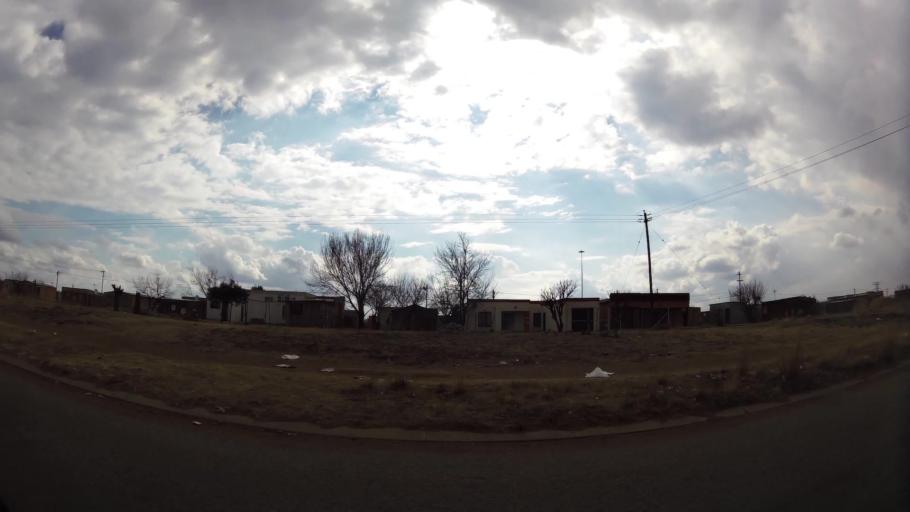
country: ZA
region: Gauteng
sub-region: Sedibeng District Municipality
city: Vanderbijlpark
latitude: -26.6795
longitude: 27.7897
